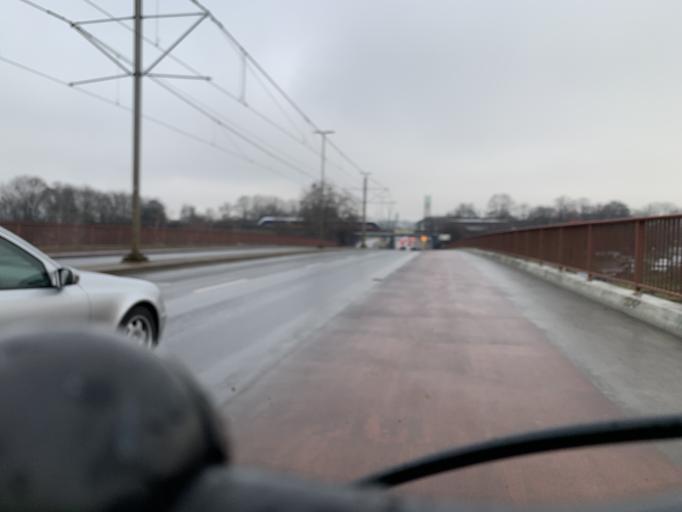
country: DE
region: North Rhine-Westphalia
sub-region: Regierungsbezirk Dusseldorf
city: Hochfeld
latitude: 51.4074
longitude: 6.7520
